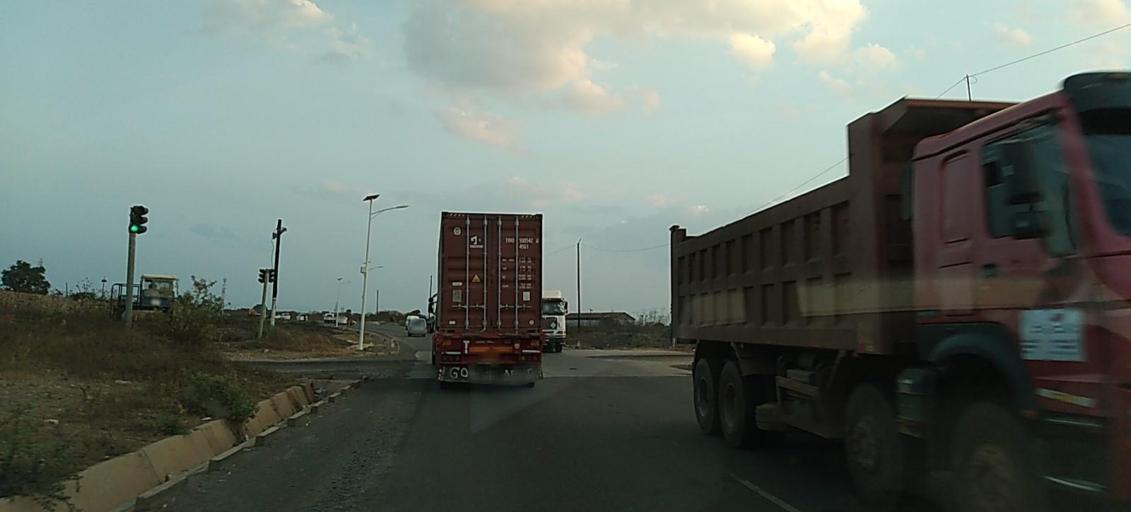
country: ZM
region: Copperbelt
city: Chingola
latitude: -12.5373
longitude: 27.8394
